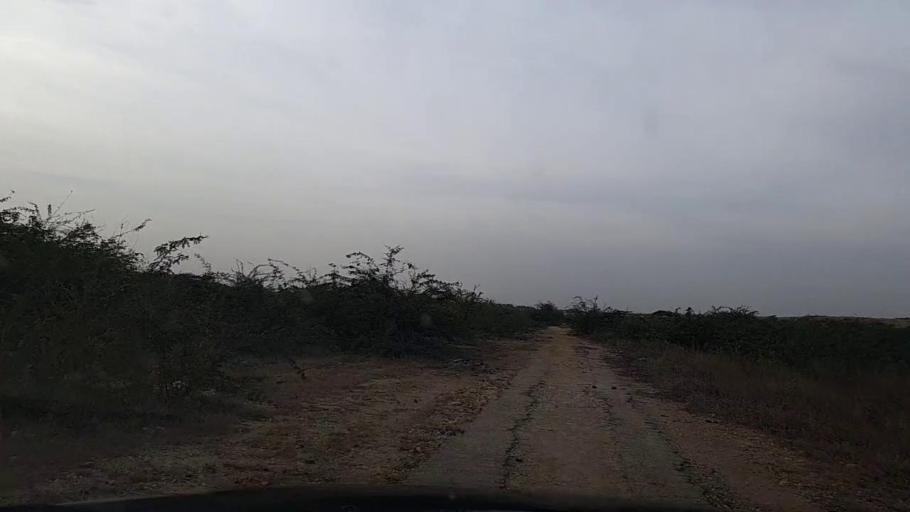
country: PK
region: Sindh
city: Gharo
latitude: 24.7882
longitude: 67.5550
